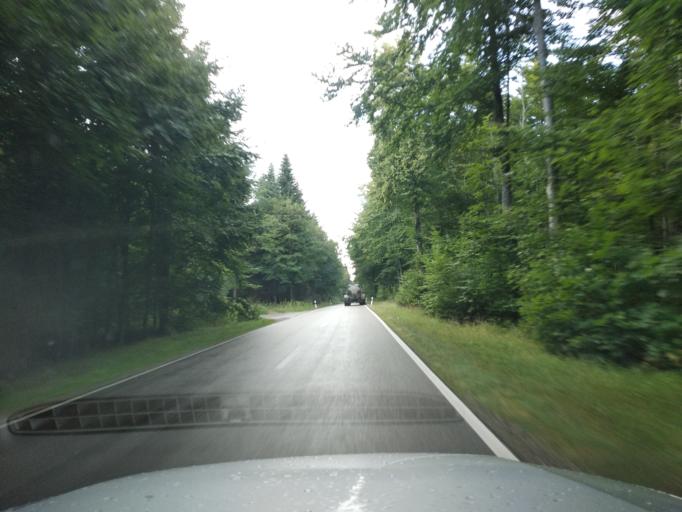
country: DE
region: Bavaria
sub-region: Swabia
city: Wolfertschwenden
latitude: 47.8656
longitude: 10.2232
